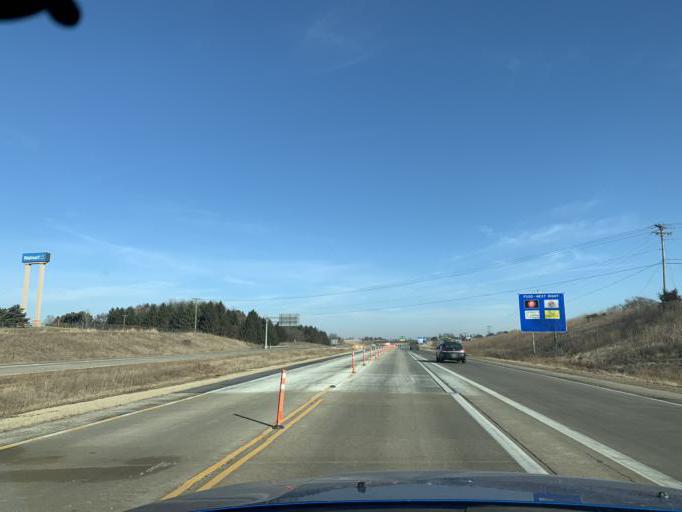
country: US
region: Wisconsin
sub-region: Green County
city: Monroe
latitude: 42.6073
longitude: -89.6623
